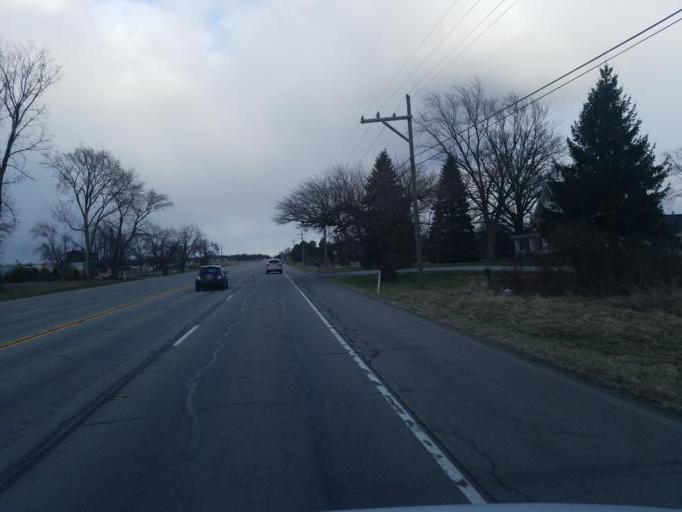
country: US
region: Indiana
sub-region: Hancock County
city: New Palestine
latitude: 39.7797
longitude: -85.8896
